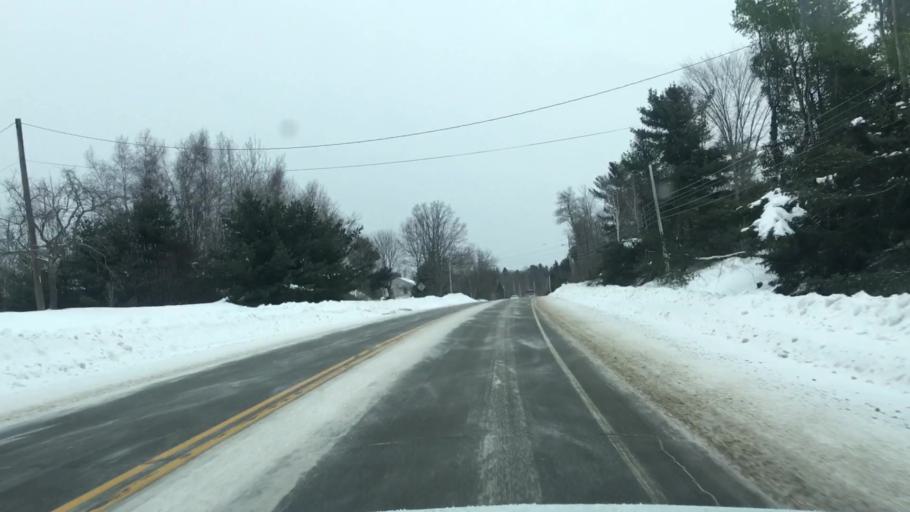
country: US
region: Maine
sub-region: Penobscot County
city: Lincoln
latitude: 45.4020
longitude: -68.4900
